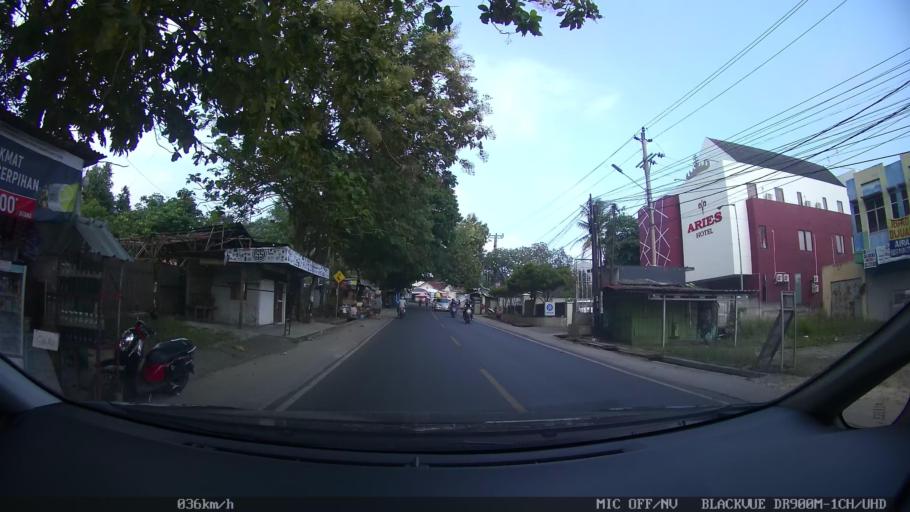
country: ID
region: Lampung
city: Kedaton
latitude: -5.3926
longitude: 105.2270
